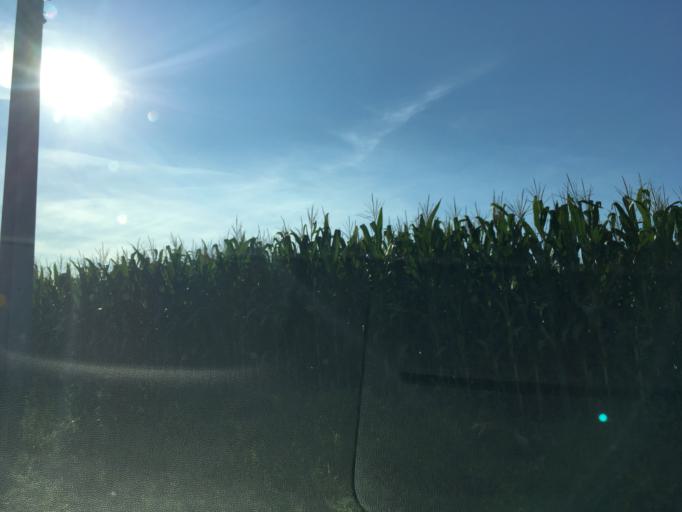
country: SK
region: Nitriansky
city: Svodin
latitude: 47.9021
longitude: 18.4121
